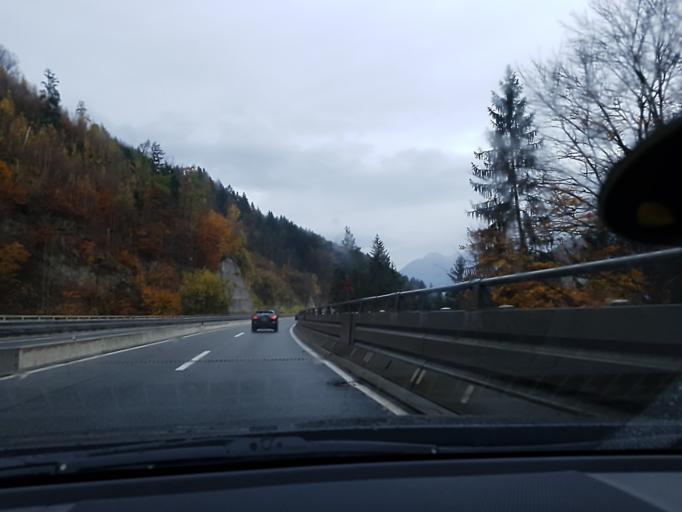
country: AT
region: Salzburg
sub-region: Politischer Bezirk Sankt Johann im Pongau
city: Bischofshofen
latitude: 47.4222
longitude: 13.2268
